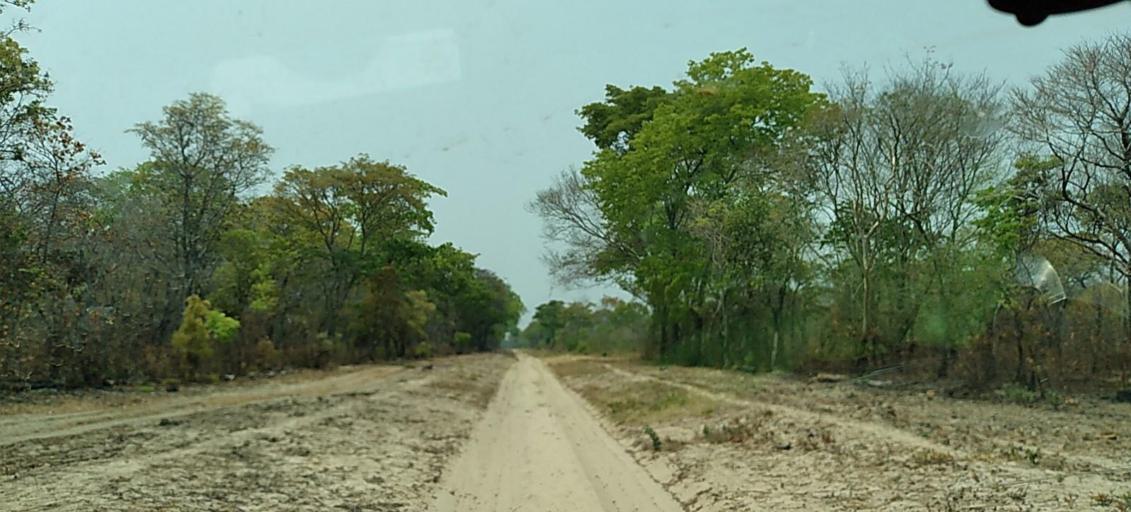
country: ZM
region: Western
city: Lukulu
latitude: -14.1403
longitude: 23.2814
